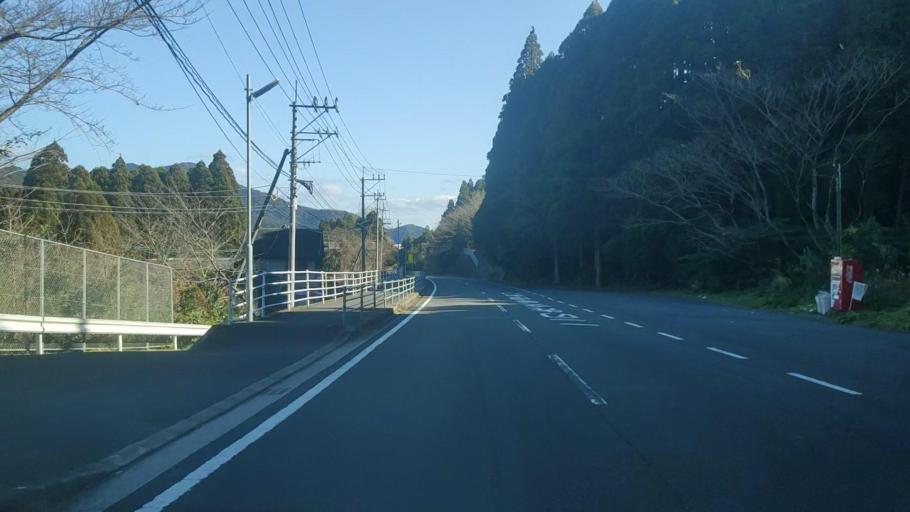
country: JP
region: Oita
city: Saiki
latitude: 32.8006
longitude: 131.9381
